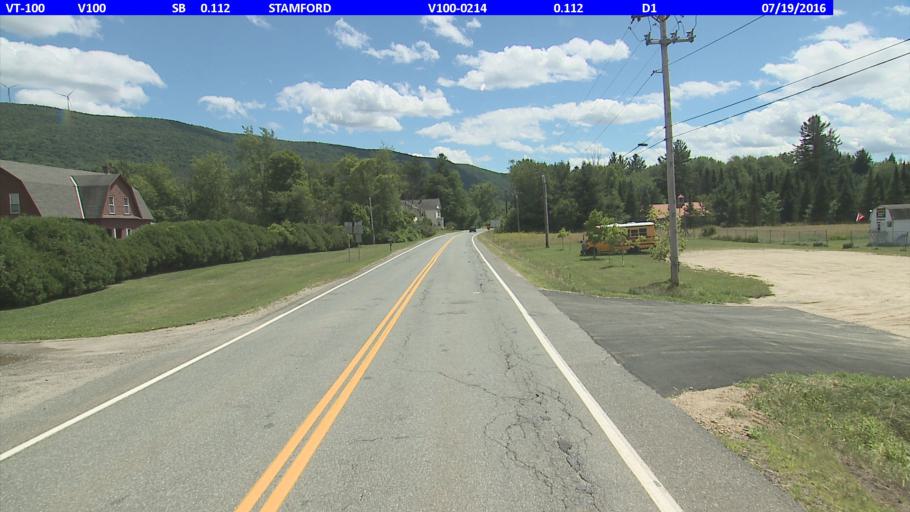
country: US
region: Massachusetts
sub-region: Berkshire County
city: North Adams
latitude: 42.7437
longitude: -73.0722
